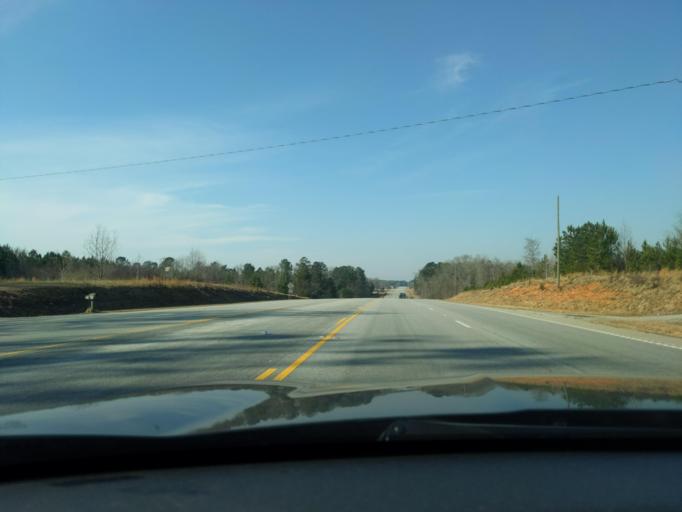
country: US
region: South Carolina
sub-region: Abbeville County
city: Abbeville
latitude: 34.1309
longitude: -82.4247
